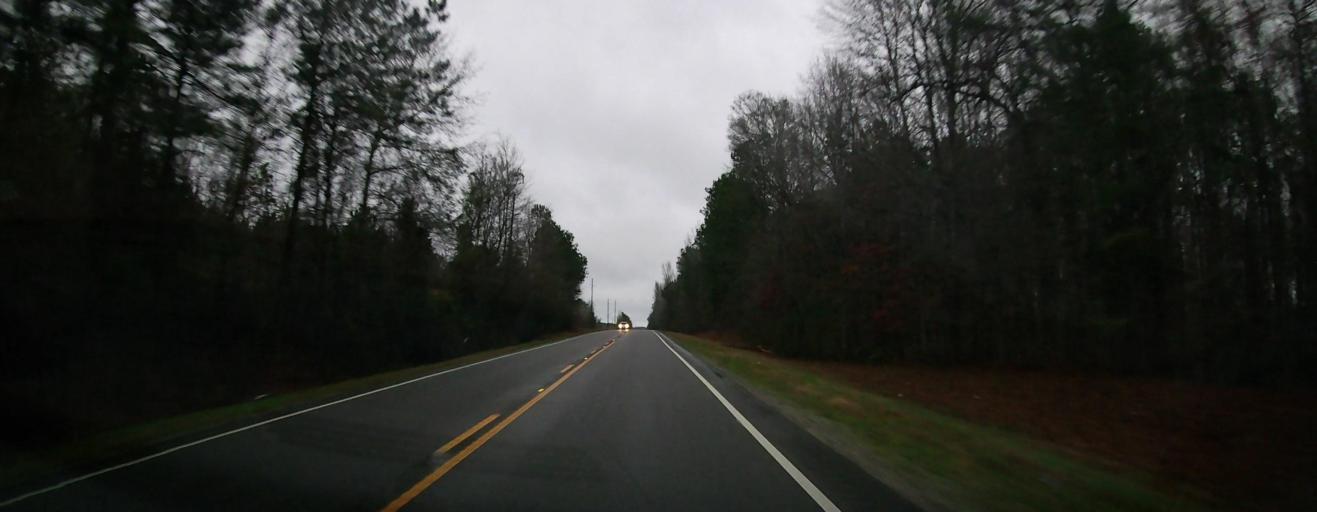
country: US
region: Alabama
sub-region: Bibb County
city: West Blocton
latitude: 33.0977
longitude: -87.1381
